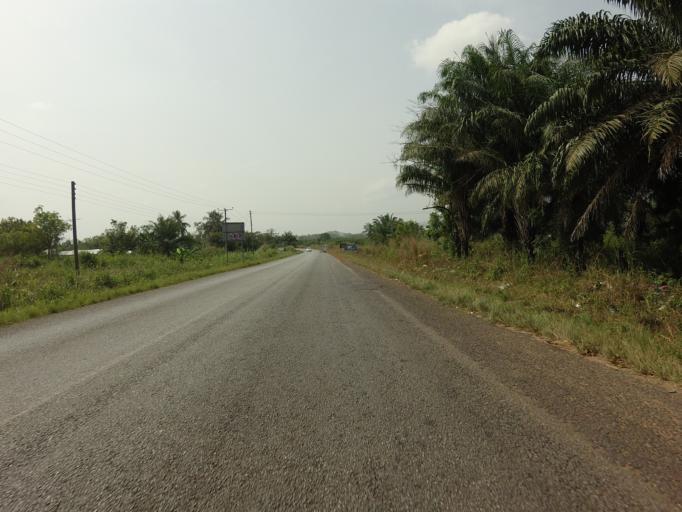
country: GH
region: Volta
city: Ho
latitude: 6.3292
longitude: 0.1648
